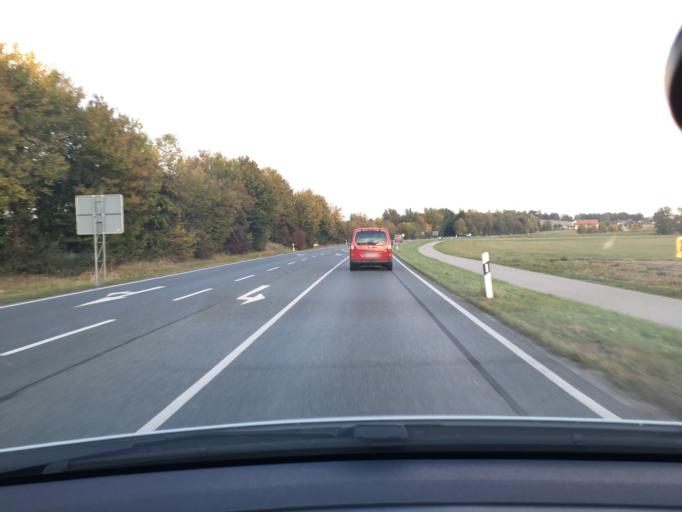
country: DE
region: Bavaria
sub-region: Regierungsbezirk Mittelfranken
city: Sachsen
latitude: 49.2844
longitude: 10.6599
